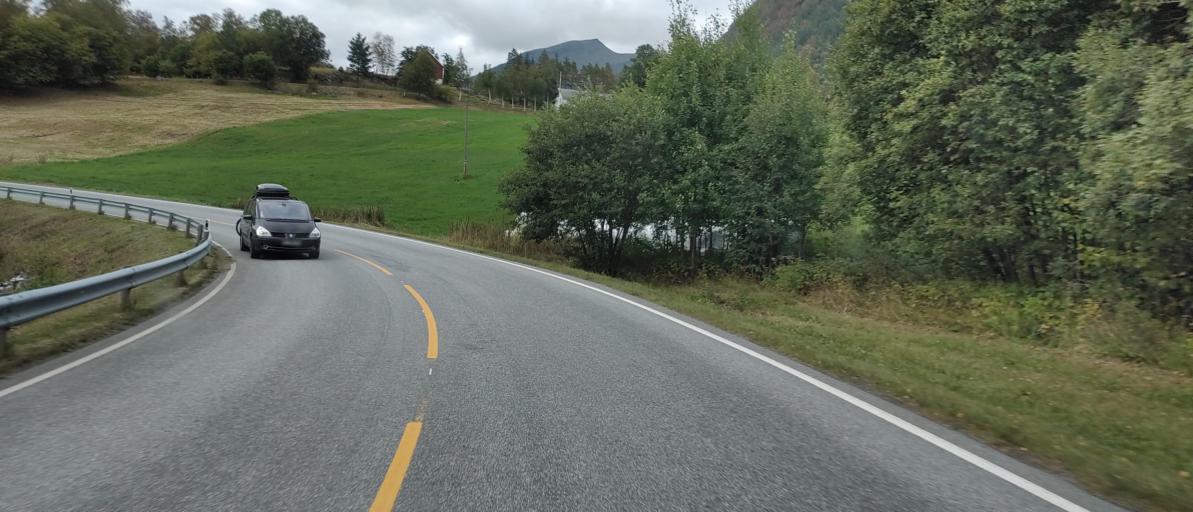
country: NO
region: More og Romsdal
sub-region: Rauma
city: Andalsnes
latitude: 62.5853
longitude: 7.5407
